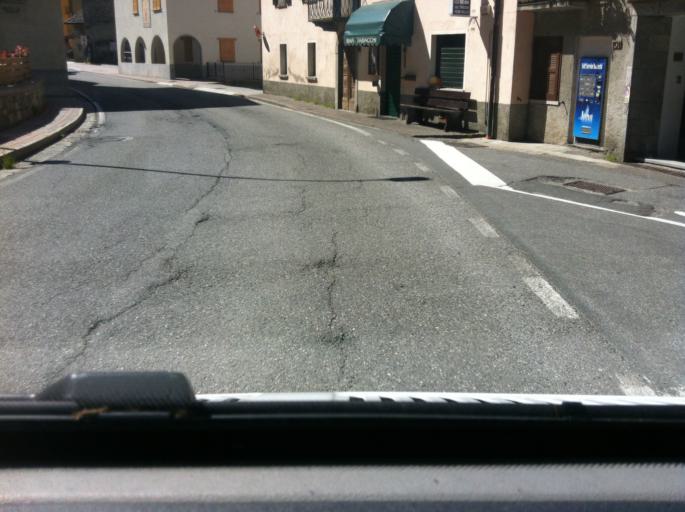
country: IT
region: Lombardy
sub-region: Provincia di Sondrio
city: Campodolcino
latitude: 46.4212
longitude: 9.3410
